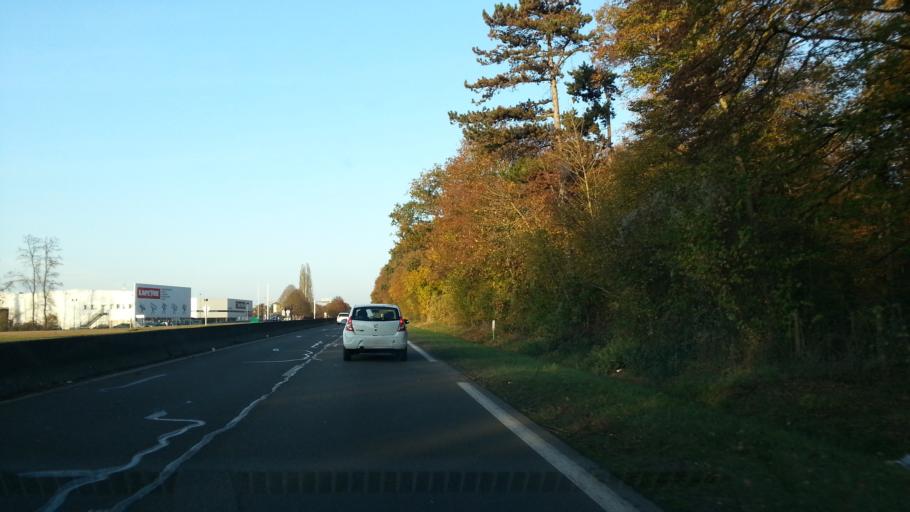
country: FR
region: Picardie
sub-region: Departement de l'Oise
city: Saint-Maximin
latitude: 49.2283
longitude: 2.4696
